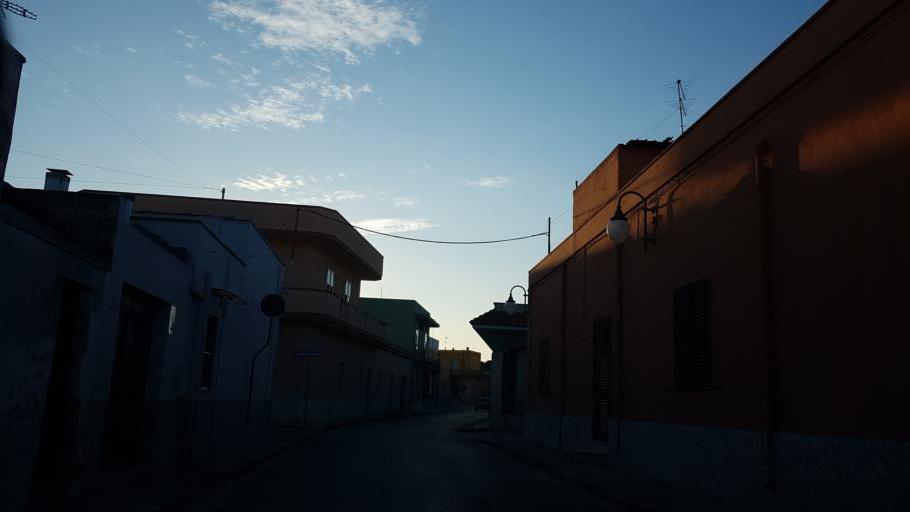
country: IT
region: Apulia
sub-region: Provincia di Brindisi
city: Tuturano
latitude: 40.5460
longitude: 17.9483
